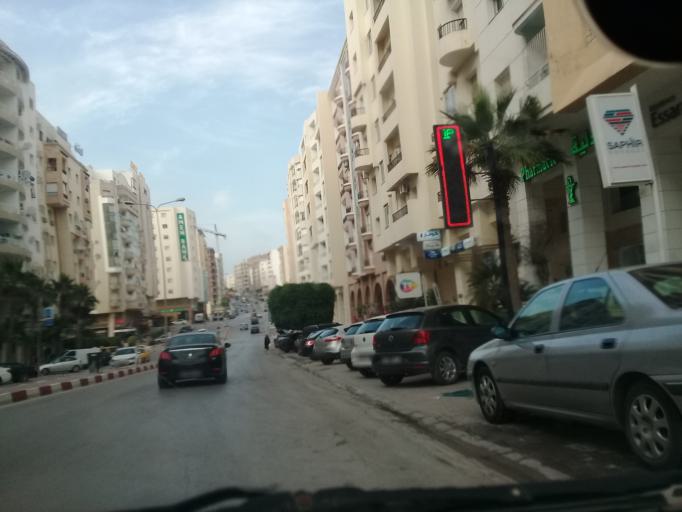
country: TN
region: Ariana
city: Ariana
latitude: 36.8649
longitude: 10.1680
